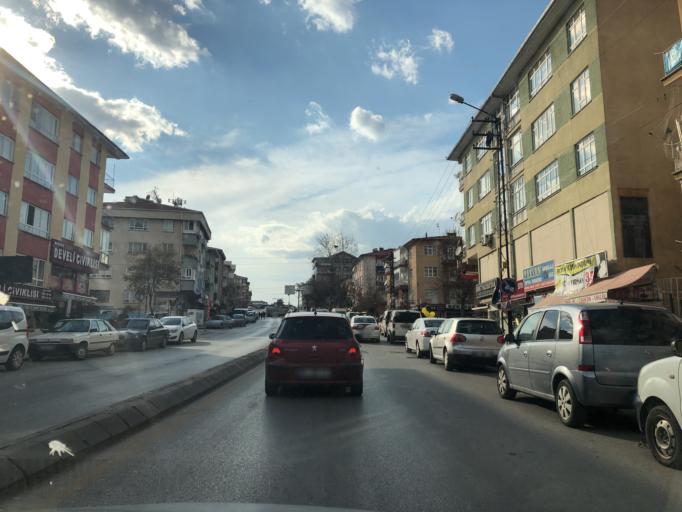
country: TR
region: Ankara
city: Ankara
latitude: 39.9845
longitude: 32.8619
